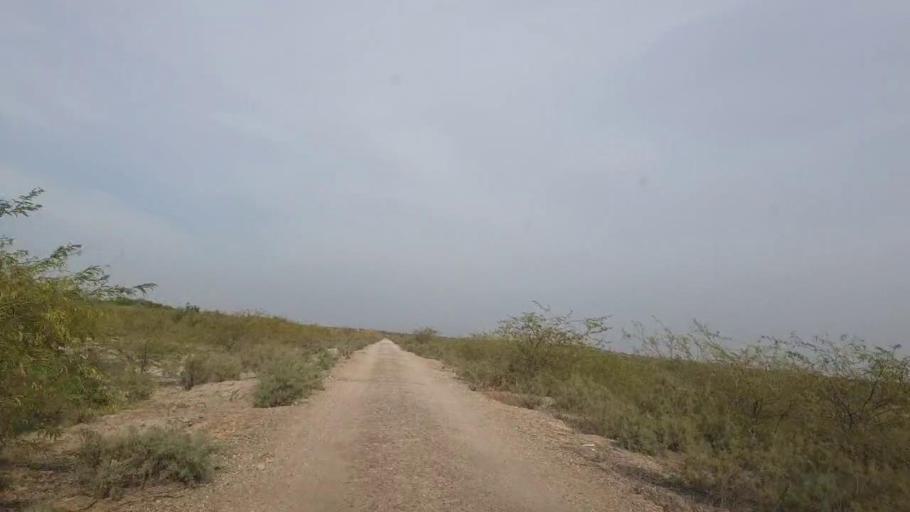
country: PK
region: Sindh
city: Nabisar
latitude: 24.9918
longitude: 69.5686
